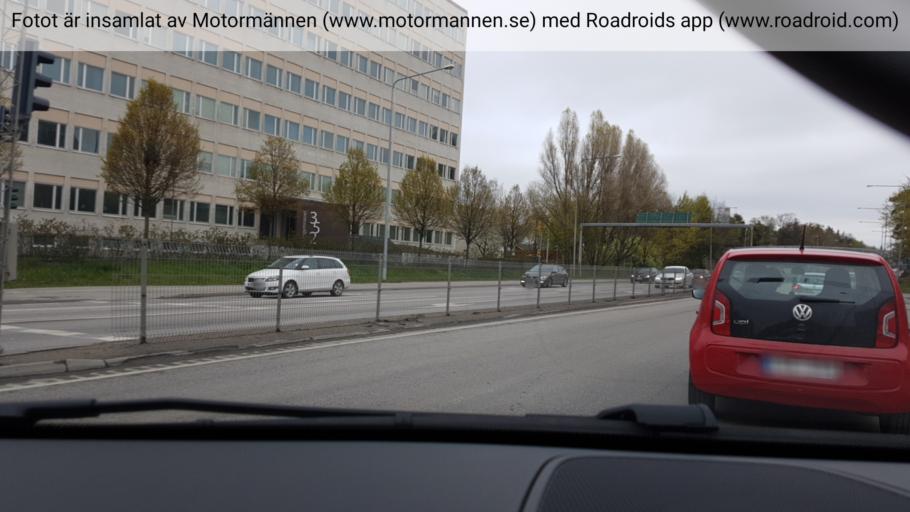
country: SE
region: Stockholm
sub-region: Huddinge Kommun
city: Huddinge
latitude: 59.2435
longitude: 17.9940
